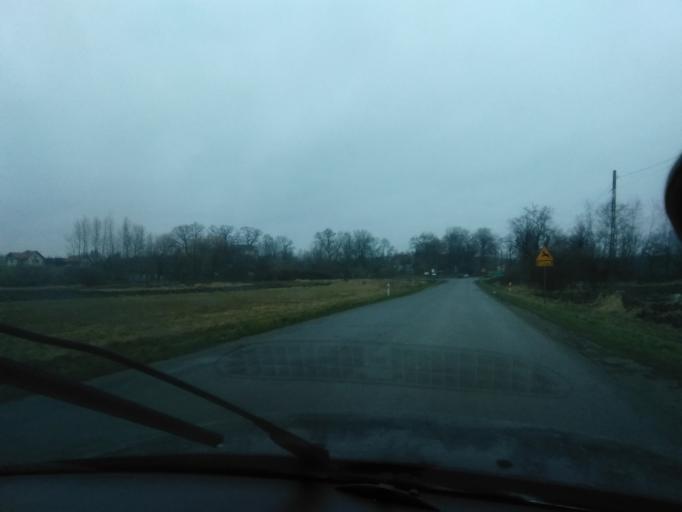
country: PL
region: Subcarpathian Voivodeship
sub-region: Powiat jaroslawski
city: Pruchnik
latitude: 49.9057
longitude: 22.5468
